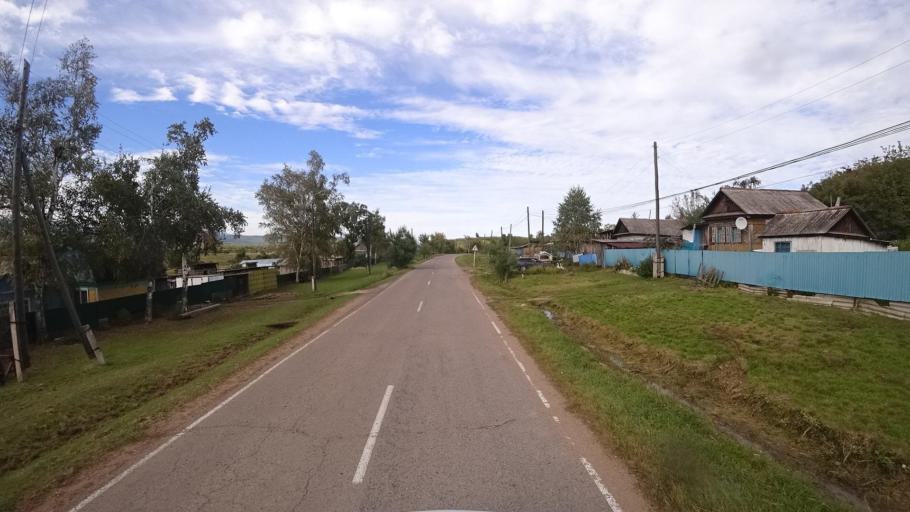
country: RU
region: Primorskiy
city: Dostoyevka
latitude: 44.3267
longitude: 133.4770
